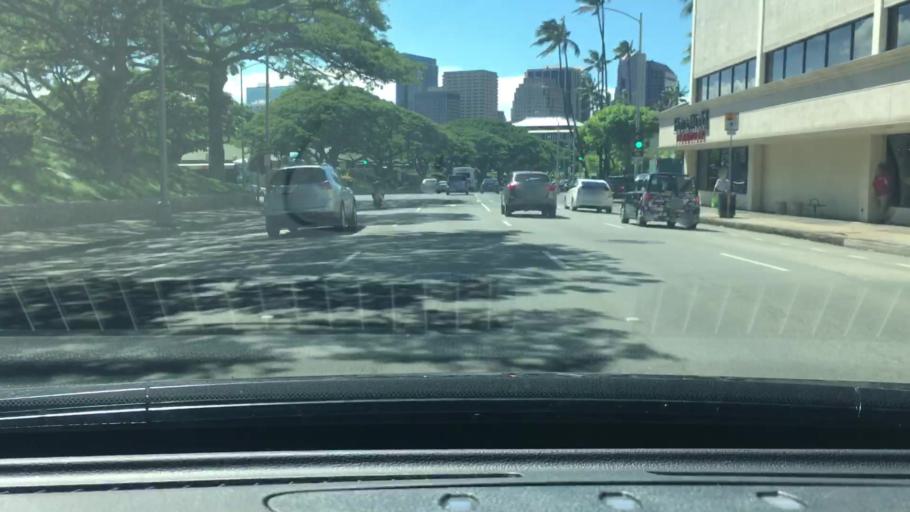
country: US
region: Hawaii
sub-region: Honolulu County
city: Honolulu
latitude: 21.3048
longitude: -157.8521
